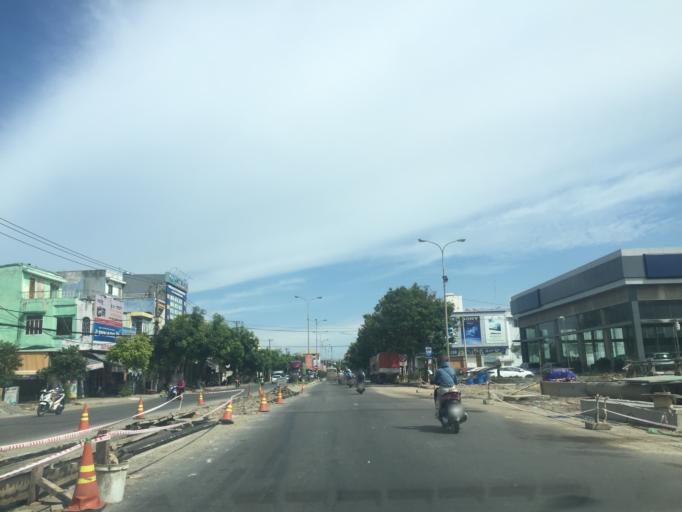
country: VN
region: Da Nang
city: Lien Chieu
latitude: 16.0604
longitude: 108.1624
